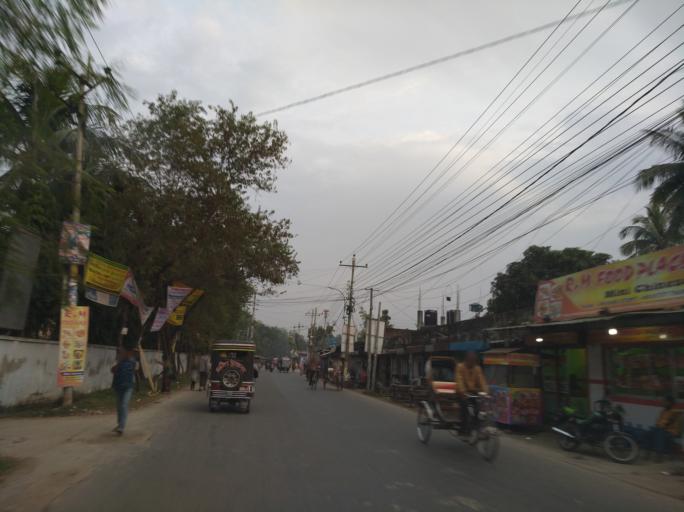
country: BD
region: Khulna
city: Khulna
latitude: 22.8425
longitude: 89.5430
